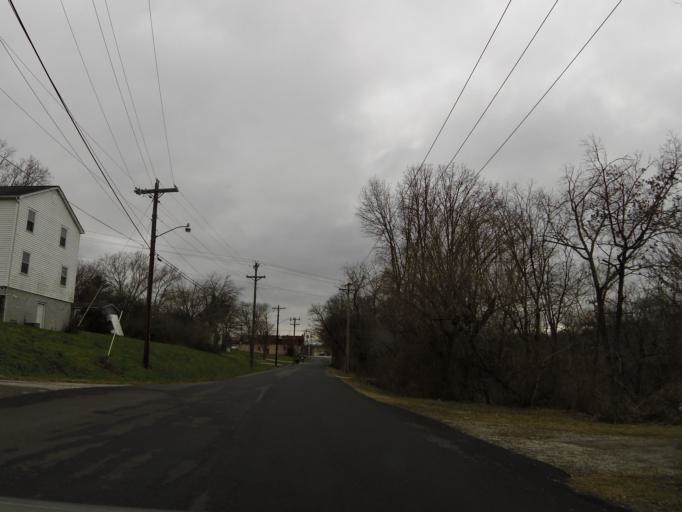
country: US
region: Tennessee
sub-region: Jefferson County
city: Jefferson City
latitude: 36.1281
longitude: -83.4880
